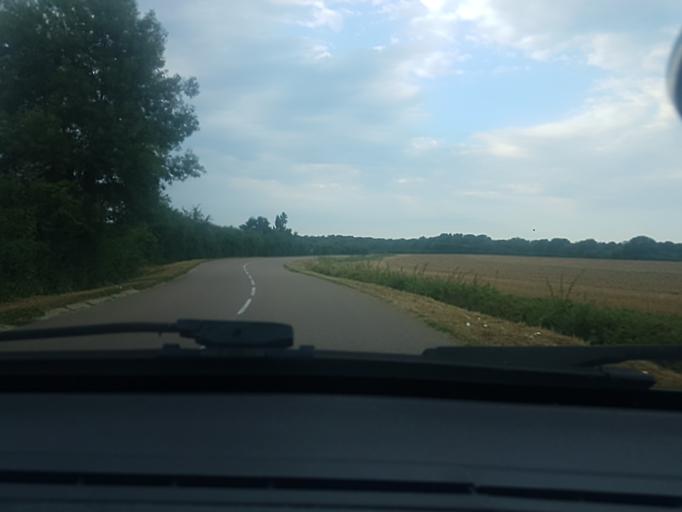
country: FR
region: Bourgogne
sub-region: Departement de Saone-et-Loire
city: Givry
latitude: 46.7358
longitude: 4.7503
